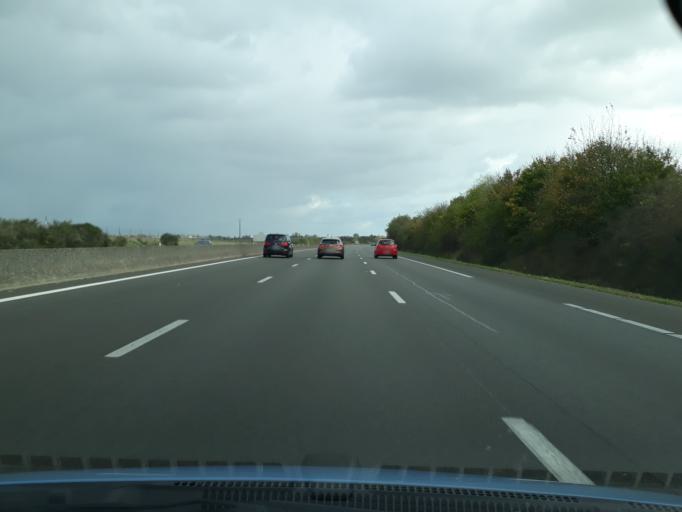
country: FR
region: Centre
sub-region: Departement du Loiret
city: La Chapelle-Saint-Mesmin
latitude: 47.9006
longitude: 1.8225
